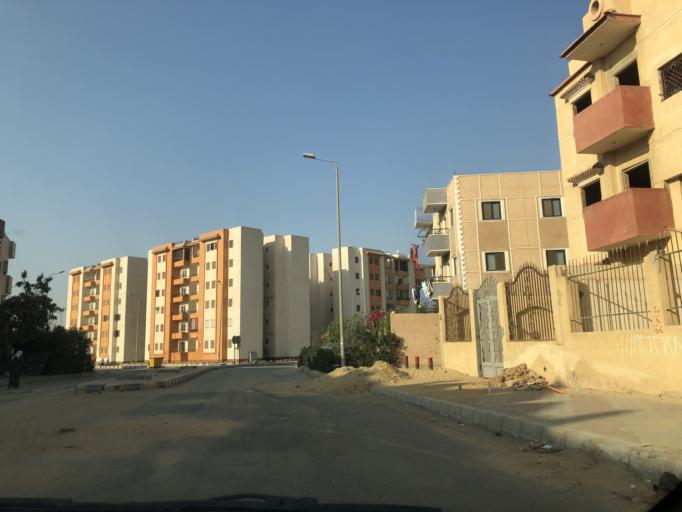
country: EG
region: Al Jizah
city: Madinat Sittah Uktubar
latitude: 29.9050
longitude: 30.9279
